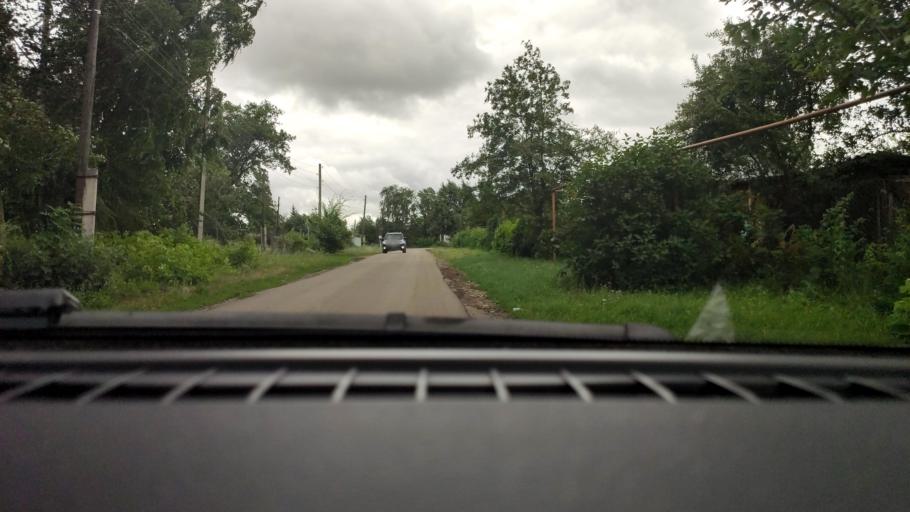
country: RU
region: Voronezj
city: Zemlyansk
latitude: 51.9060
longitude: 38.7273
